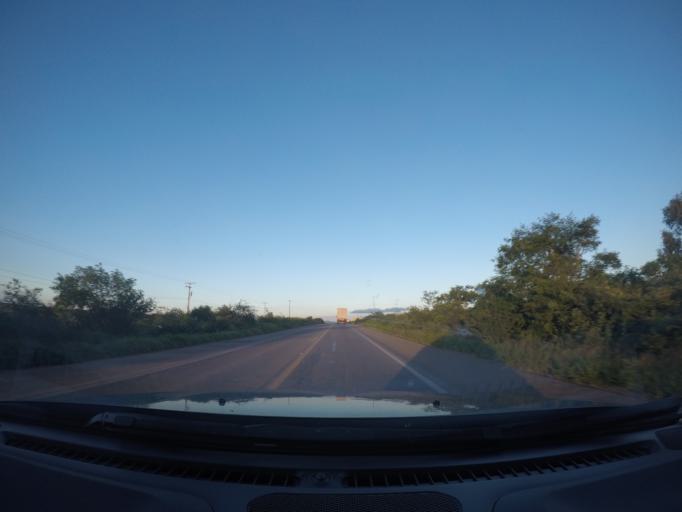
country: BR
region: Bahia
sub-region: Seabra
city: Seabra
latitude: -12.4172
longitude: -41.9823
